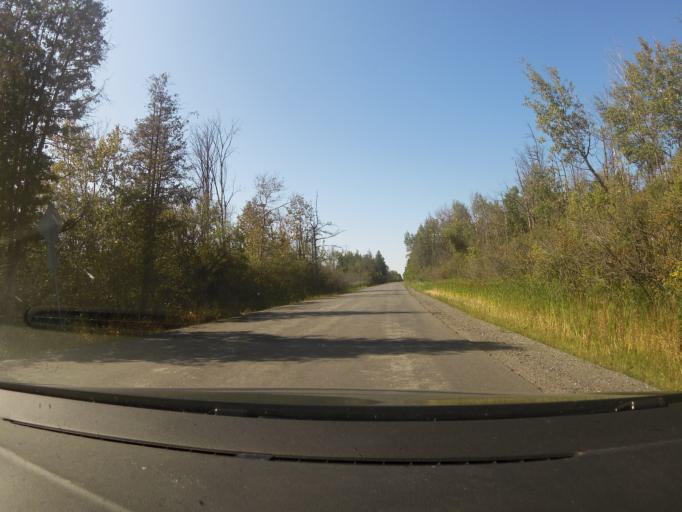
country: CA
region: Ontario
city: Bells Corners
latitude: 45.2997
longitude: -76.0267
